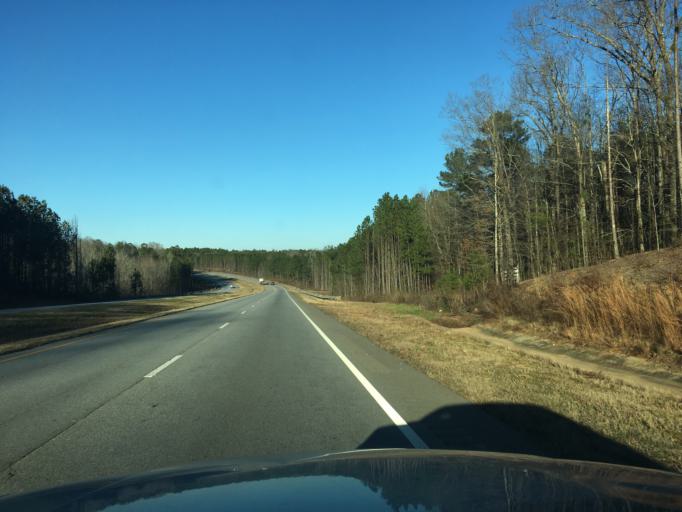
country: US
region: Georgia
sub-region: Carroll County
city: Carrollton
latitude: 33.4447
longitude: -85.1275
